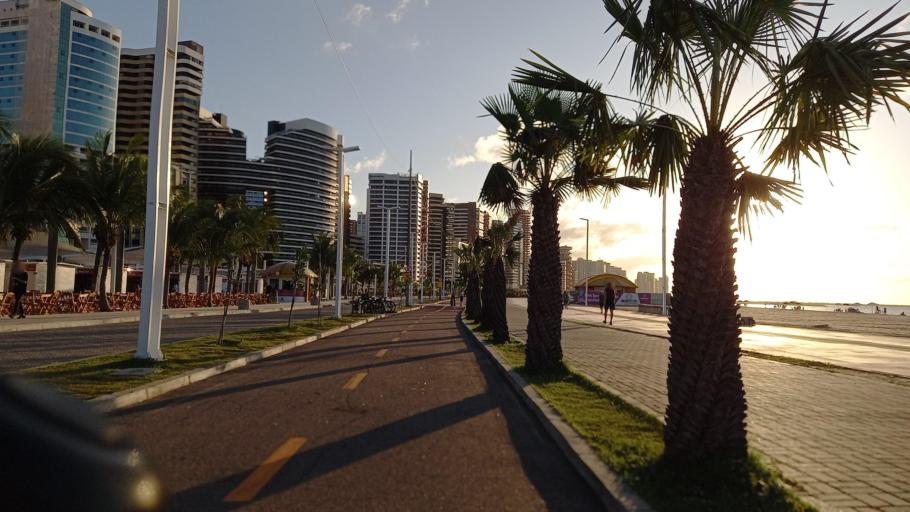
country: BR
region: Ceara
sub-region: Fortaleza
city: Fortaleza
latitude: -3.7249
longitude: -38.4960
